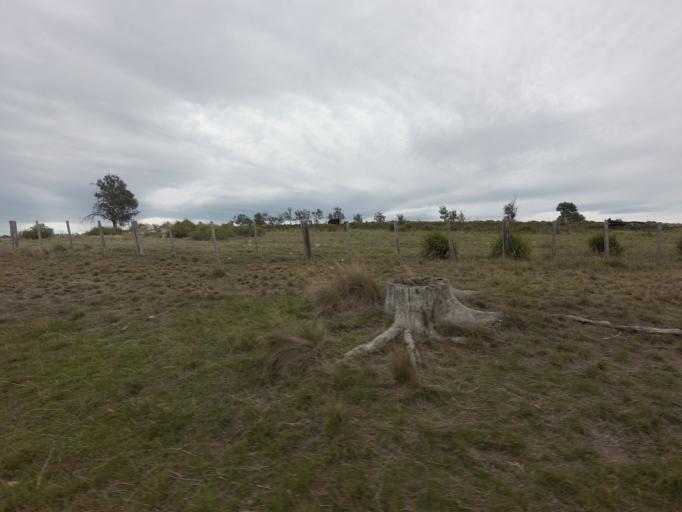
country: AU
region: Tasmania
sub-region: Derwent Valley
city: New Norfolk
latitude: -42.3953
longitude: 146.8822
